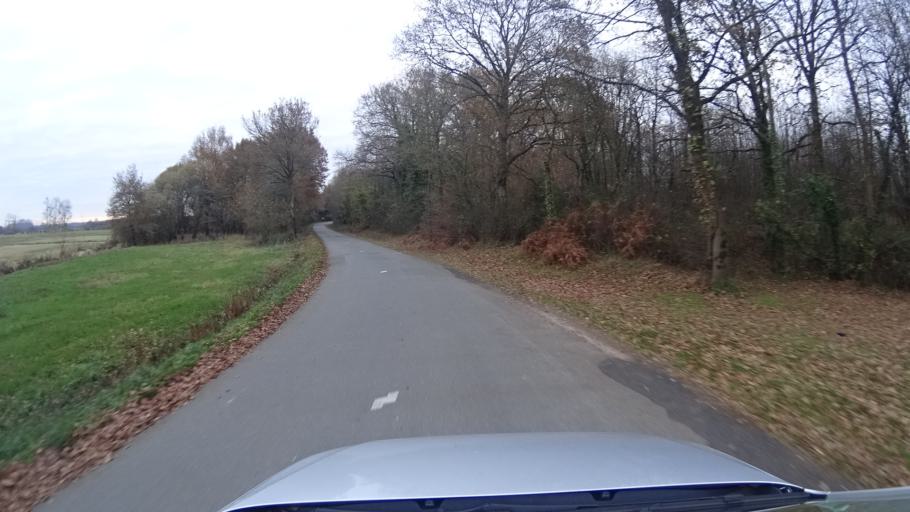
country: FR
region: Pays de la Loire
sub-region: Departement de la Loire-Atlantique
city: Avessac
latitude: 47.6785
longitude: -1.9256
